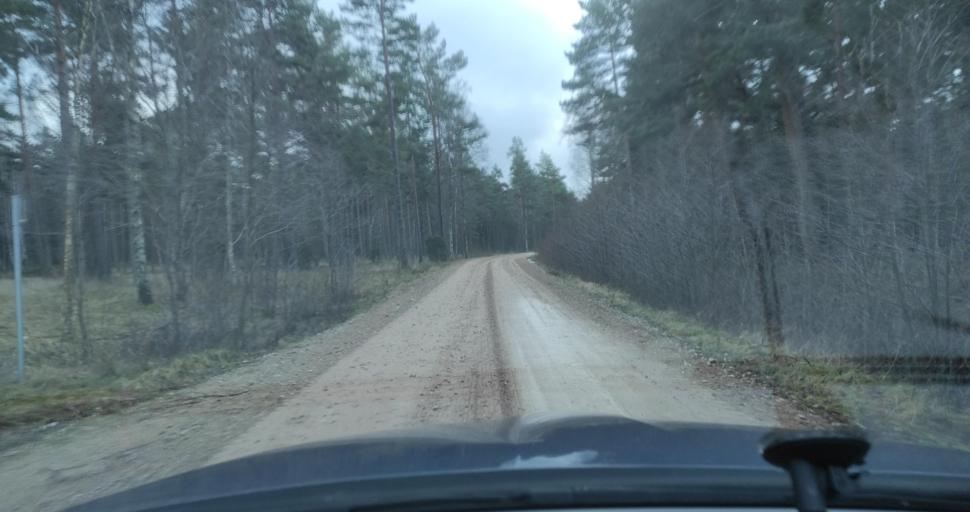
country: LV
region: Pavilostas
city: Pavilosta
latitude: 56.8363
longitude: 21.0752
